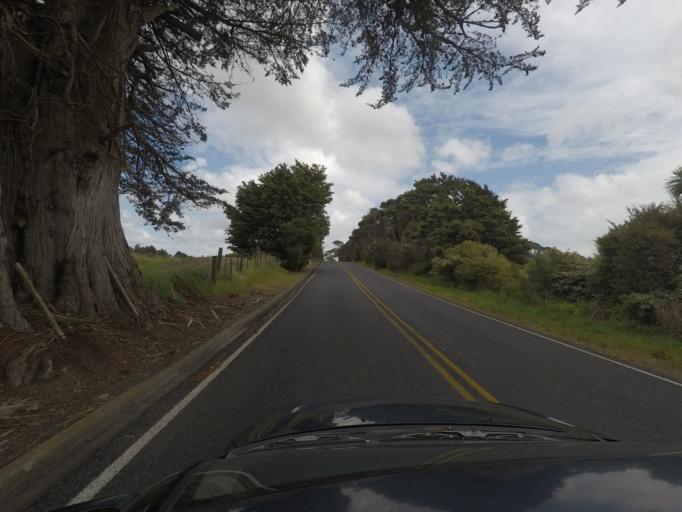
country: NZ
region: Auckland
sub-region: Auckland
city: Parakai
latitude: -36.6500
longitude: 174.5204
